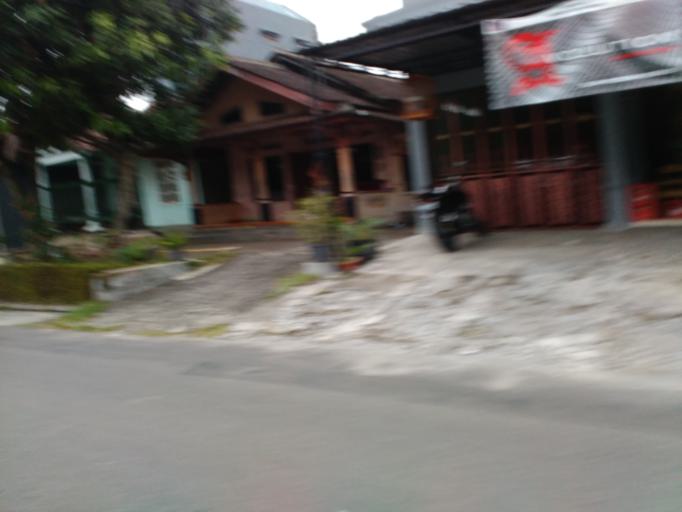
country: ID
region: Central Java
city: Boyolali
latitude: -7.5231
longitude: 110.5947
